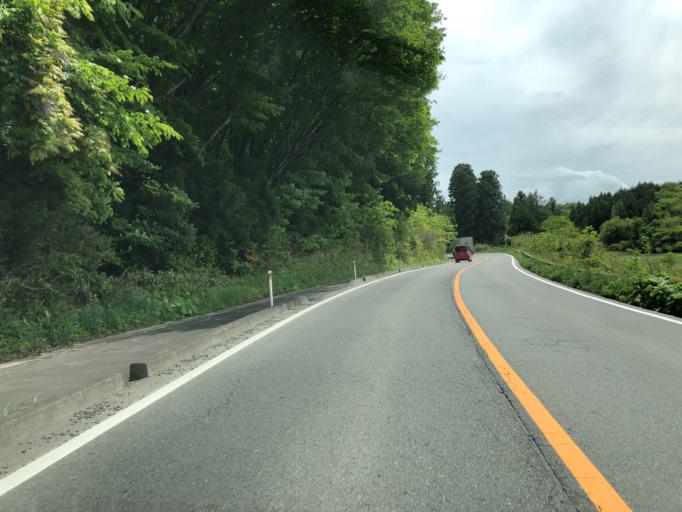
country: JP
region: Fukushima
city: Ishikawa
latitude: 37.0902
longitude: 140.3538
